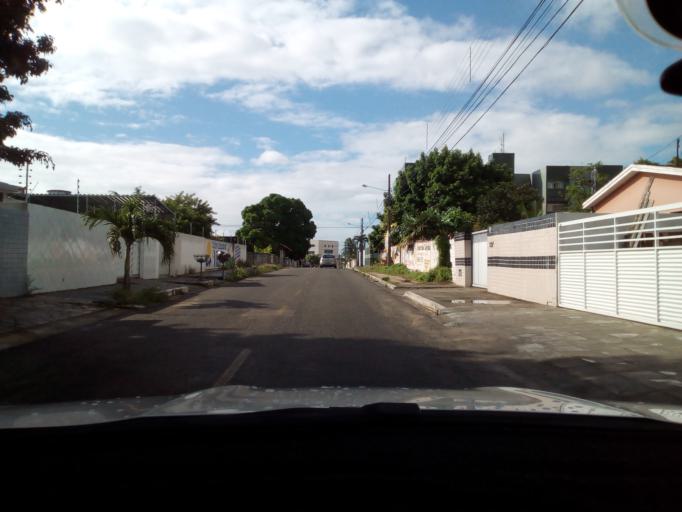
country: BR
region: Paraiba
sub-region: Joao Pessoa
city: Joao Pessoa
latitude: -7.1680
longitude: -34.8701
